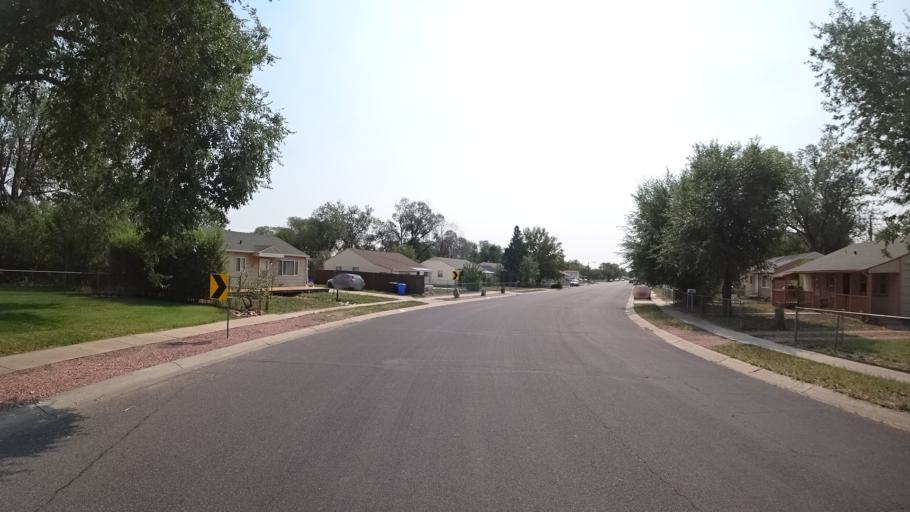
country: US
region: Colorado
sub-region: El Paso County
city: Colorado Springs
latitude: 38.8036
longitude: -104.8083
